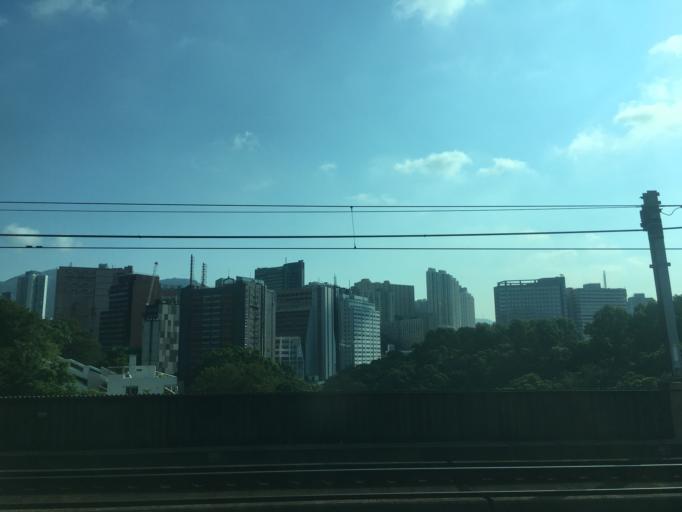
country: HK
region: Tsuen Wan
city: Tsuen Wan
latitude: 22.3548
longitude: 114.1175
